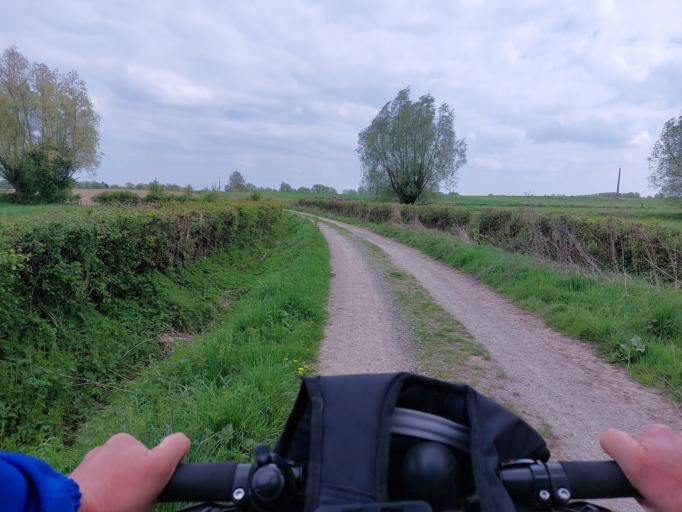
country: FR
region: Nord-Pas-de-Calais
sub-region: Departement du Nord
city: La Longueville
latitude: 50.2918
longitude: 3.8343
